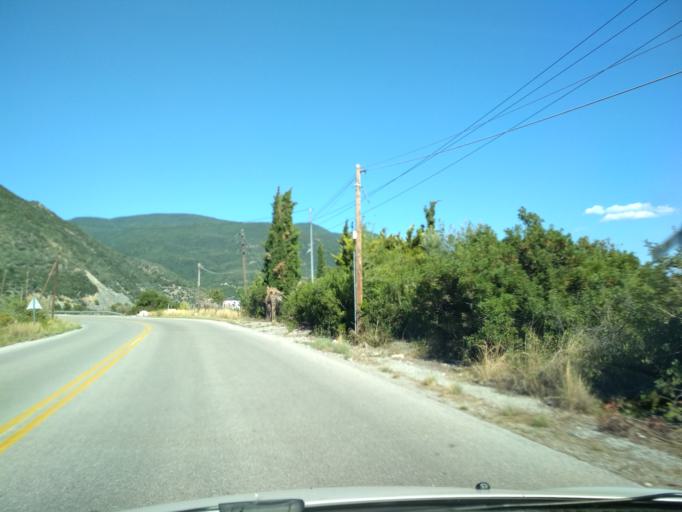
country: GR
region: Central Greece
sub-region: Nomos Evvoias
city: Oreoi
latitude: 38.8477
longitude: 23.1208
